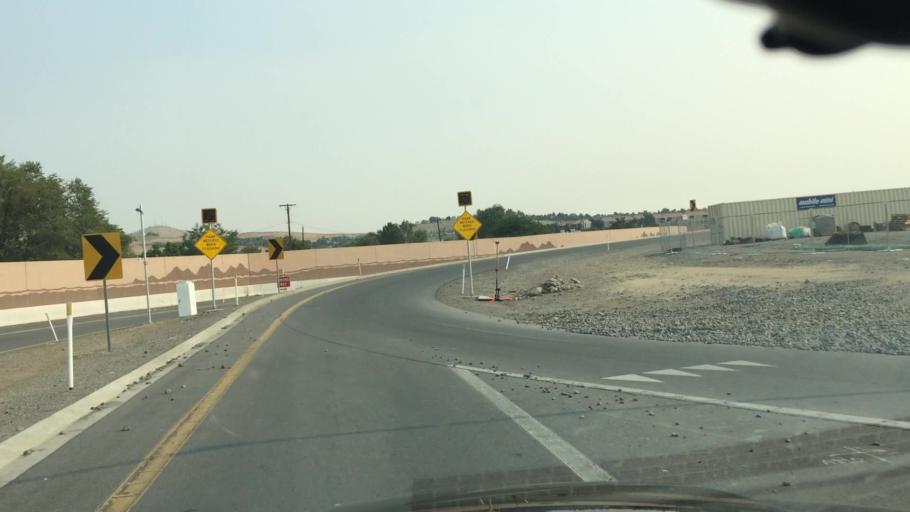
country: US
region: Nevada
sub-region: Washoe County
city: Reno
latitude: 39.5457
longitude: -119.7892
